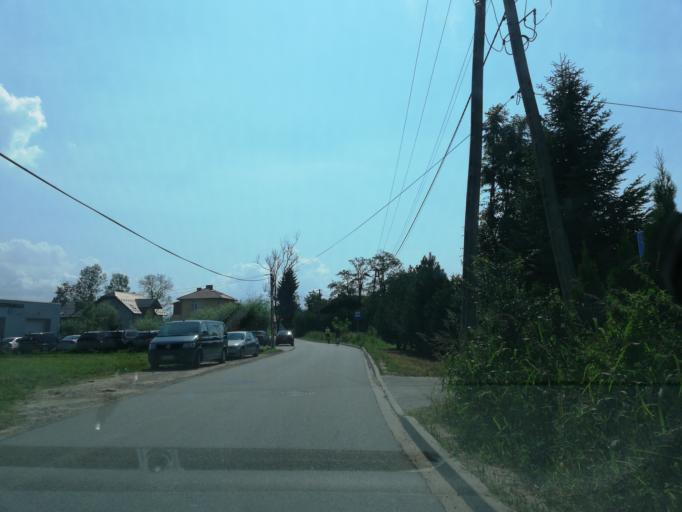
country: PL
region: Lesser Poland Voivodeship
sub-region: Powiat nowosadecki
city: Chelmiec
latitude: 49.6400
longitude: 20.6772
